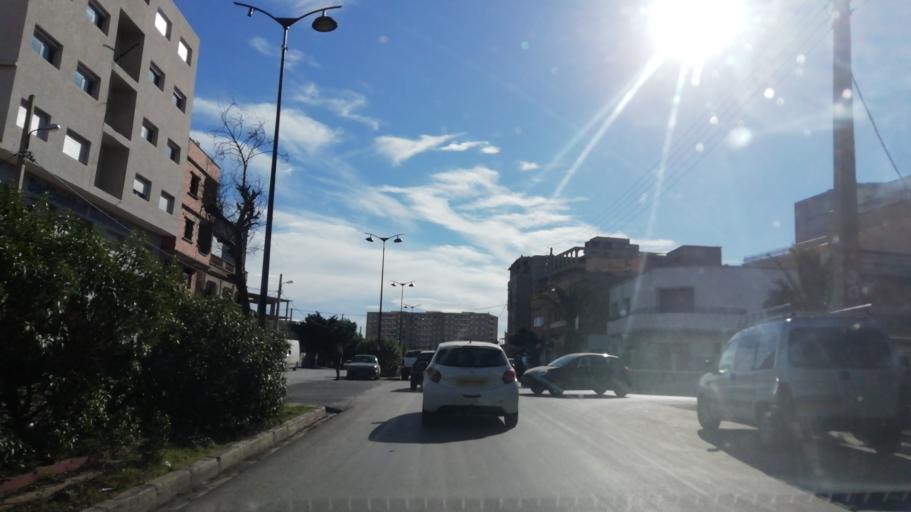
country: DZ
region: Oran
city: Oran
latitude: 35.6924
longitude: -0.6205
